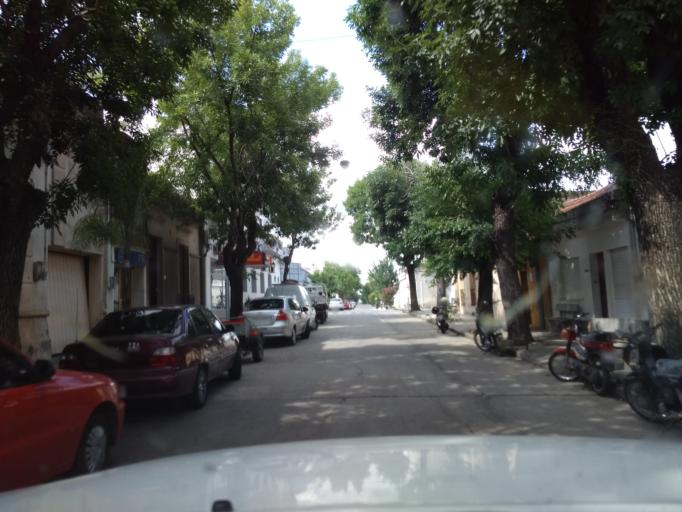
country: UY
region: Florida
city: Florida
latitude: -34.0974
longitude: -56.2145
